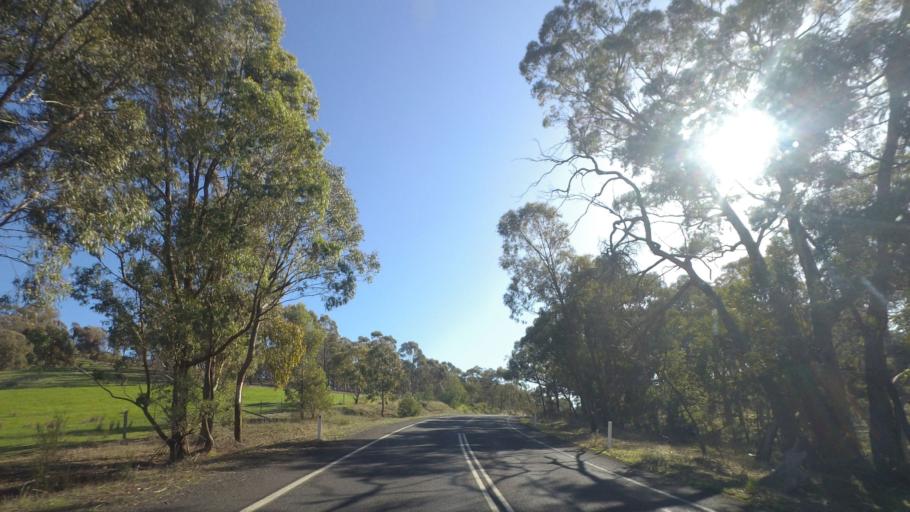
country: AU
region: Victoria
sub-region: Greater Bendigo
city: Kennington
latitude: -36.9178
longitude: 144.3356
